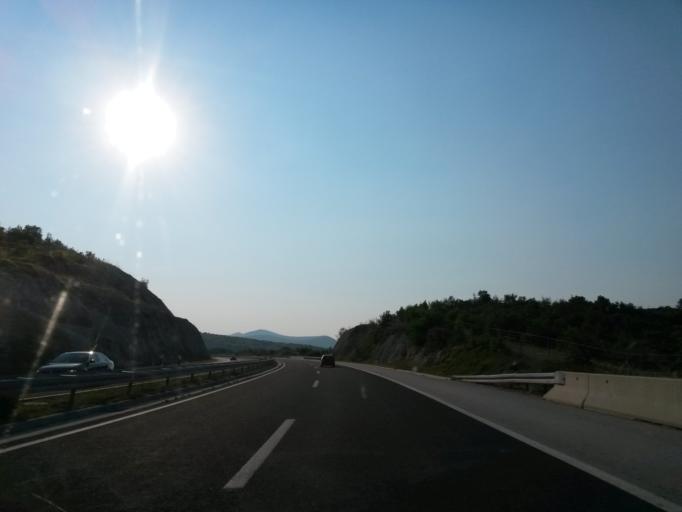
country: HR
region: Splitsko-Dalmatinska
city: Dugopolje
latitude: 43.5863
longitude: 16.6403
